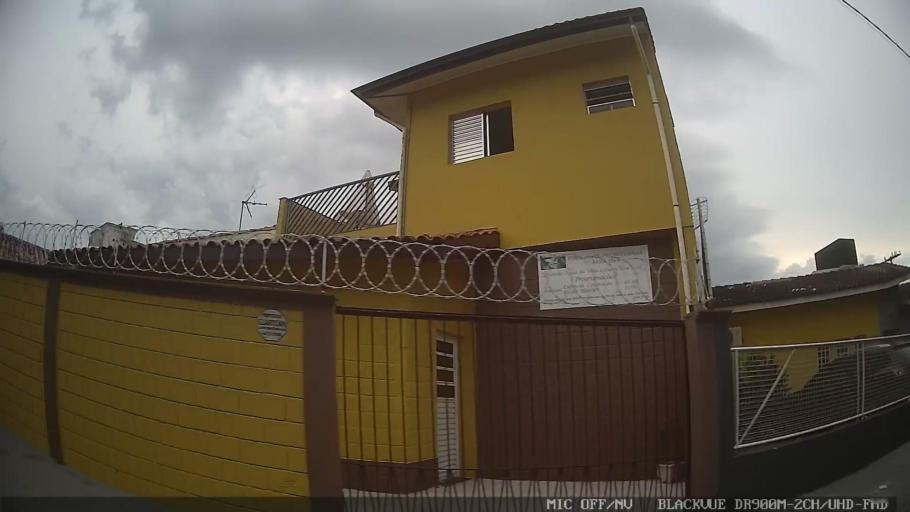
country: BR
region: Sao Paulo
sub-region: Atibaia
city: Atibaia
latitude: -23.1289
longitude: -46.5557
